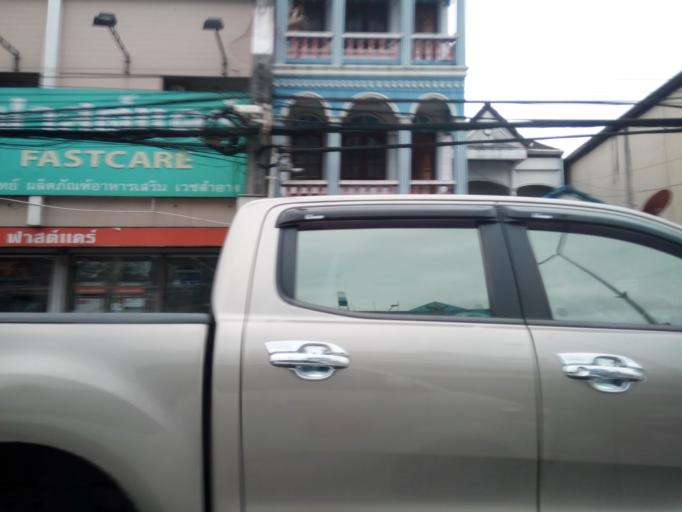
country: TH
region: Phuket
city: Thalang
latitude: 8.0275
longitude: 98.3330
